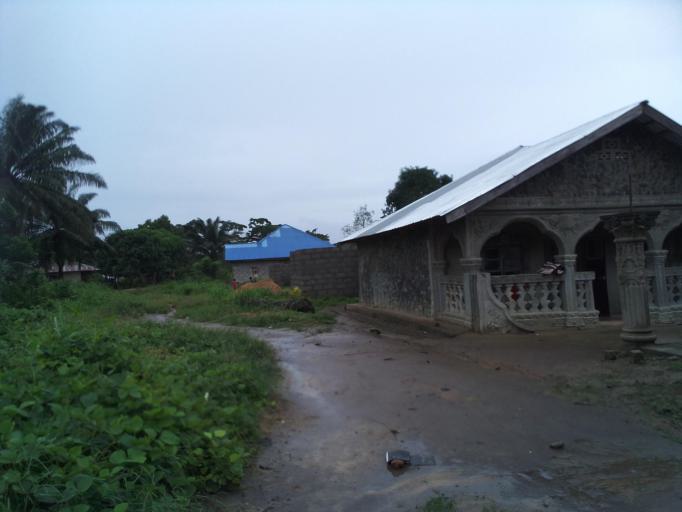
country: SL
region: Eastern Province
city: Kenema
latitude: 7.8749
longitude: -11.1608
